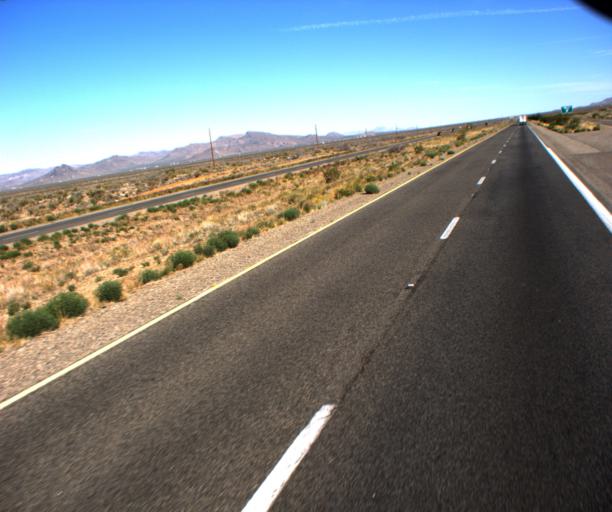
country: US
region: Arizona
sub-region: Mohave County
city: Golden Valley
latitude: 35.2916
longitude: -114.1829
